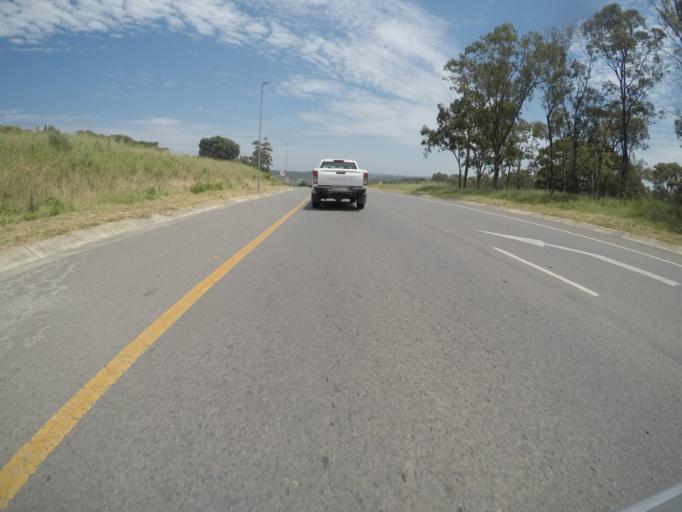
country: ZA
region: Eastern Cape
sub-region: Buffalo City Metropolitan Municipality
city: East London
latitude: -32.9395
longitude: 27.9509
